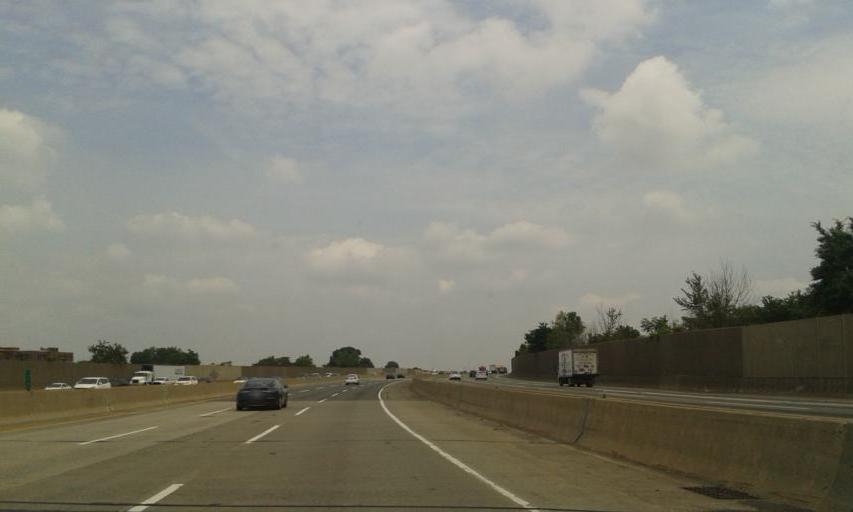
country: US
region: New Jersey
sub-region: Union County
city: Elizabeth
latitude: 40.6484
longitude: -74.2013
